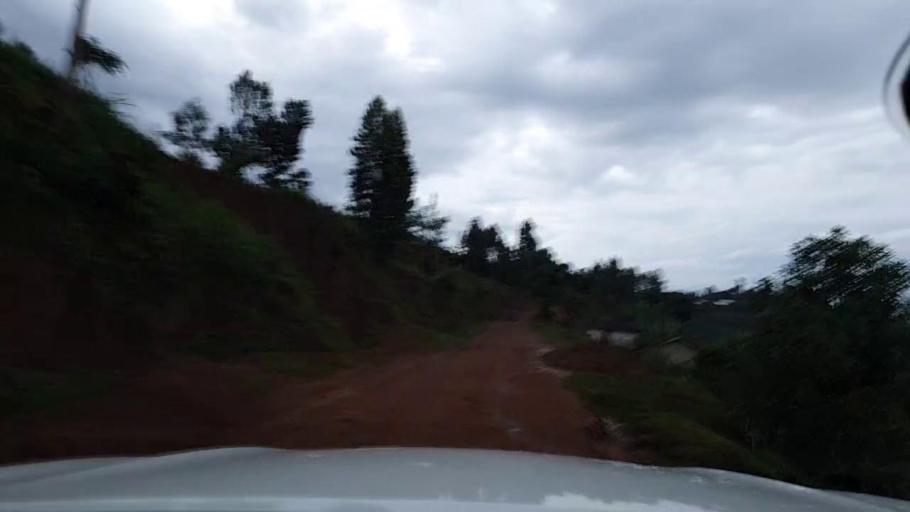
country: BI
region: Kayanza
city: Kayanza
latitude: -2.7164
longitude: 29.5430
